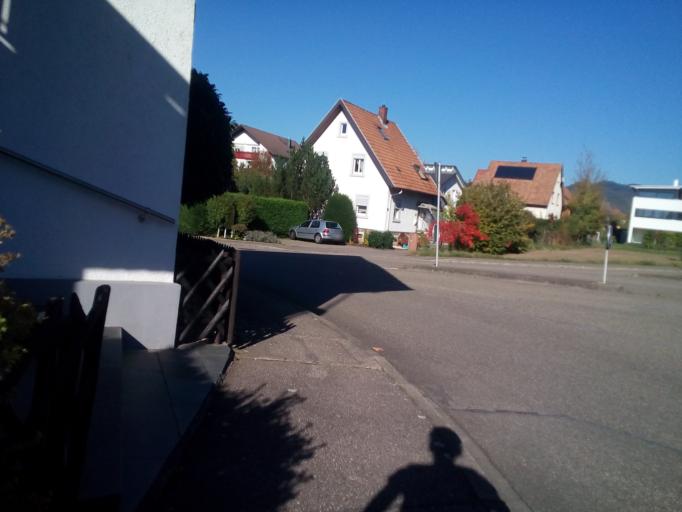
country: DE
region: Baden-Wuerttemberg
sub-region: Karlsruhe Region
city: Buhl
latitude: 48.6866
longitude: 8.1402
